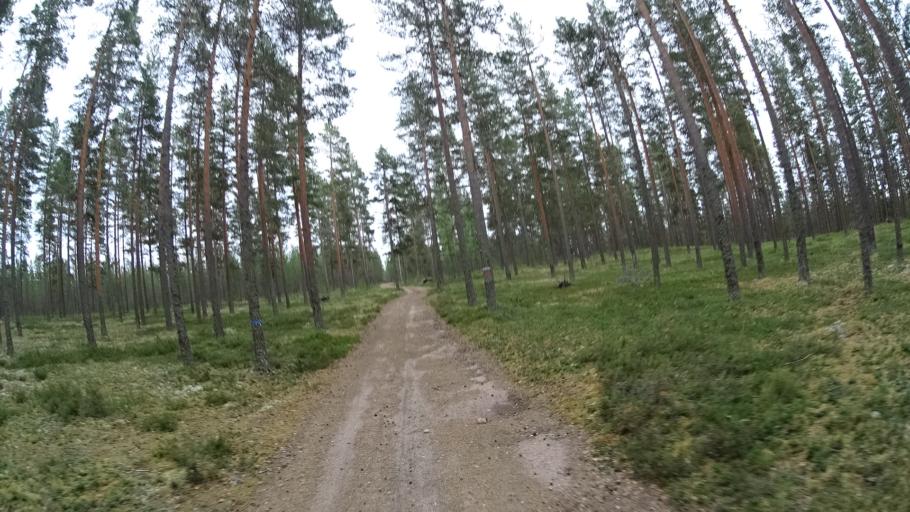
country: FI
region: Satakunta
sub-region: Pohjois-Satakunta
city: Jaemijaervi
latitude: 61.7634
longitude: 22.7703
